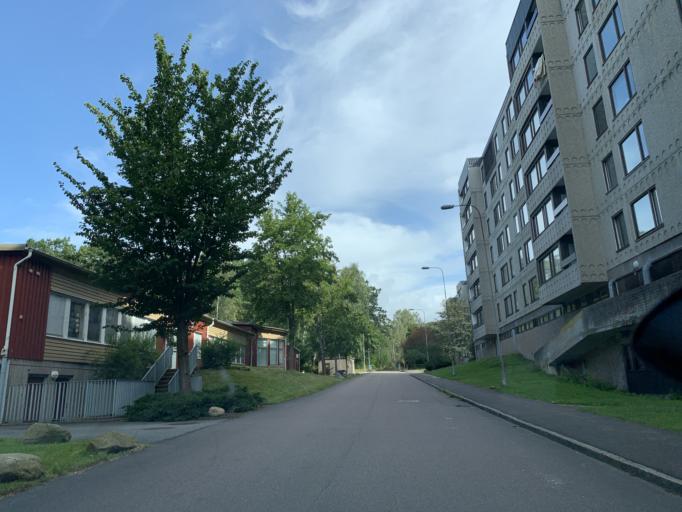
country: SE
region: Vaestra Goetaland
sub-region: Goteborg
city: Hammarkullen
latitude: 57.7694
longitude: 12.0134
